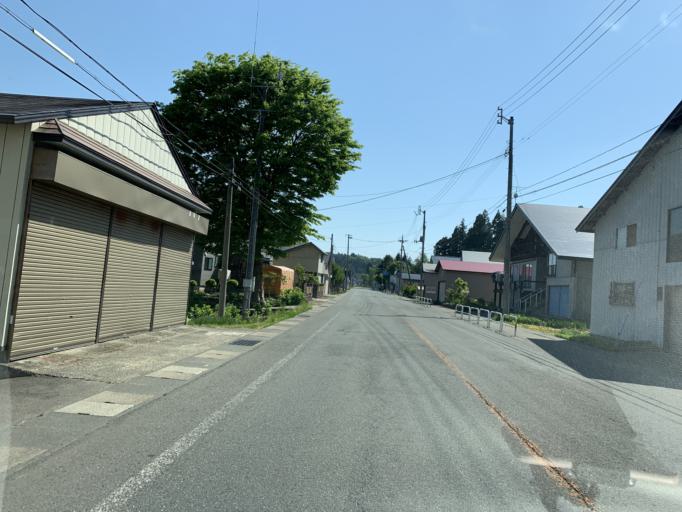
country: JP
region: Akita
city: Yokotemachi
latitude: 39.4257
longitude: 140.7476
